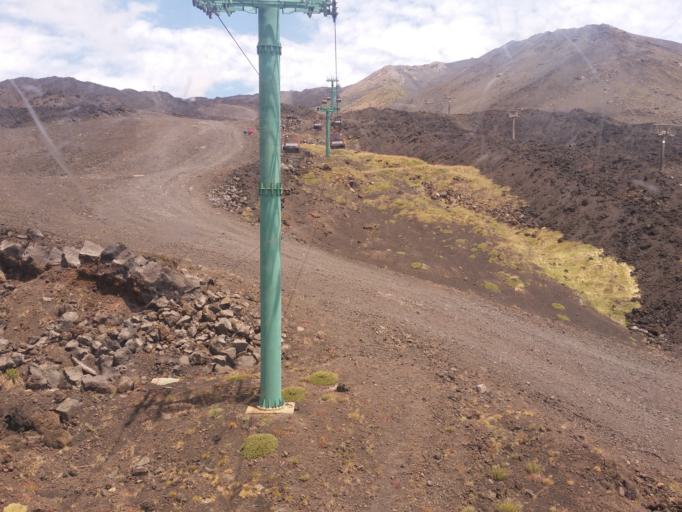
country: IT
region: Sicily
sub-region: Catania
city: Ragalna
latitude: 37.7032
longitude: 14.9992
